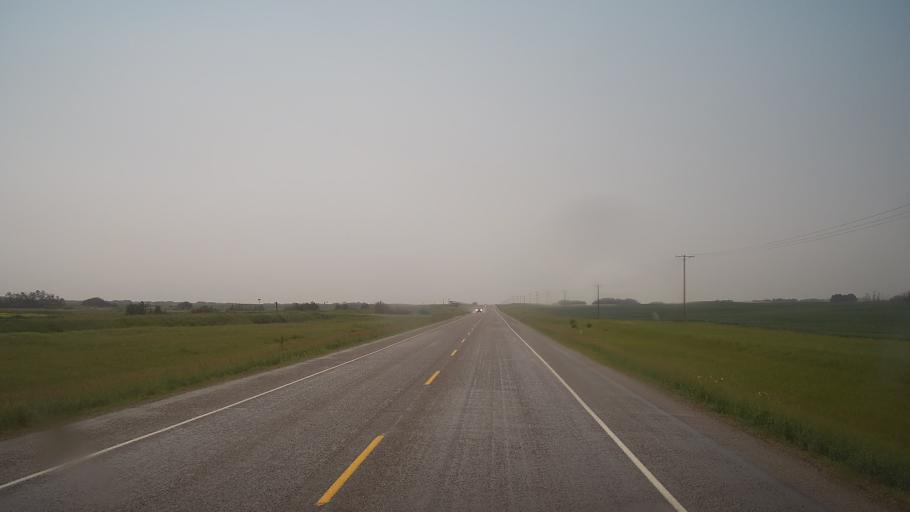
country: CA
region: Saskatchewan
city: Biggar
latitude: 52.1546
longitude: -108.2503
